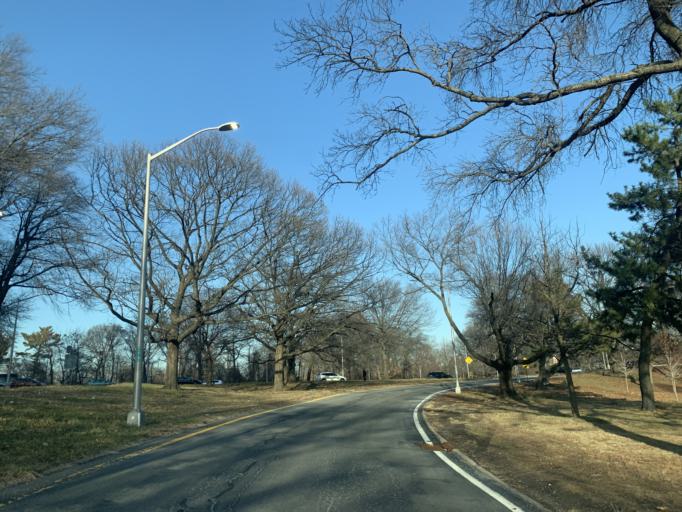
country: US
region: New York
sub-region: Bronx
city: The Bronx
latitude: 40.8553
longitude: -73.8348
